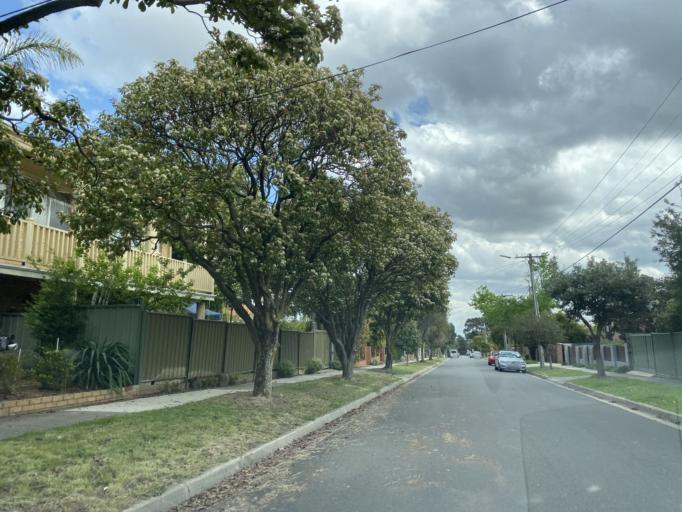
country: AU
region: Victoria
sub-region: Whitehorse
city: Burwood
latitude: -37.8598
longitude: 145.1219
